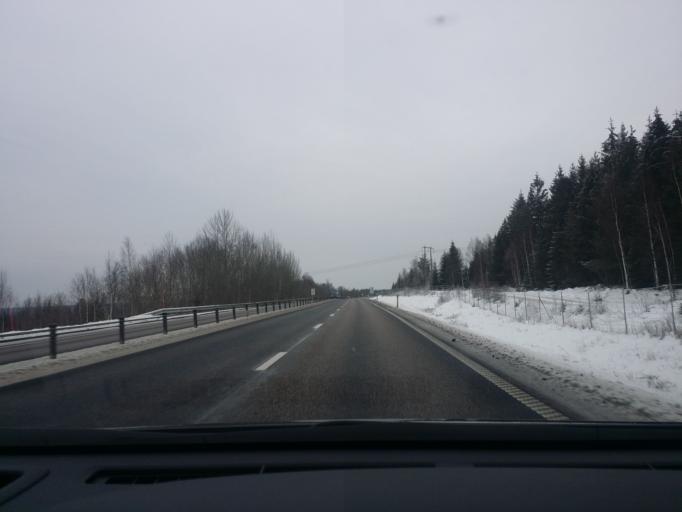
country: SE
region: Vaestra Goetaland
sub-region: Toreboda Kommun
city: Toereboda
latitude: 58.7856
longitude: 14.0140
